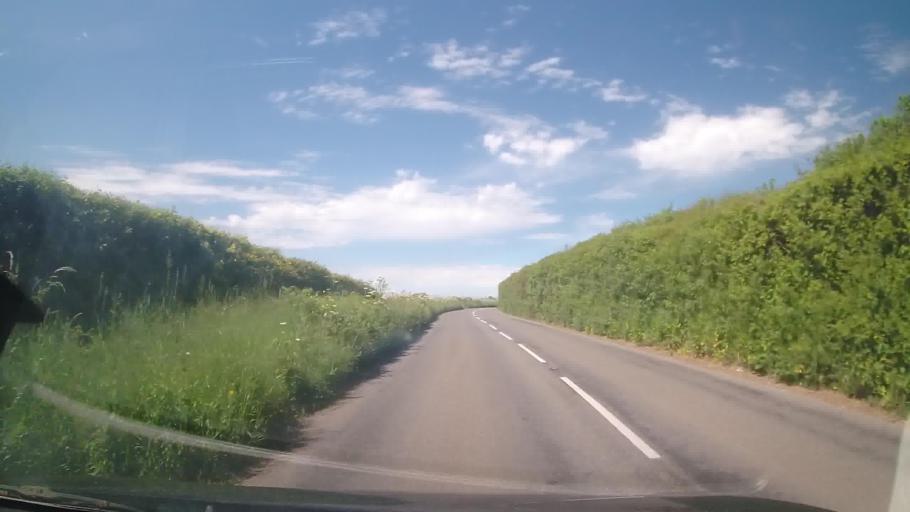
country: GB
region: England
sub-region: Devon
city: Kingsbridge
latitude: 50.2713
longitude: -3.7282
